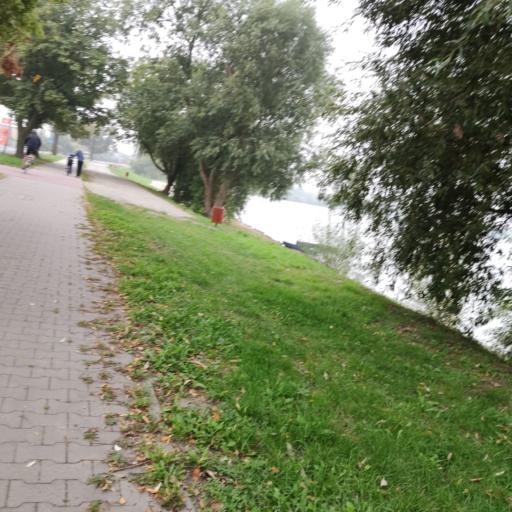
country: PL
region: Kujawsko-Pomorskie
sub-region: Powiat zninski
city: Znin
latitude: 52.8558
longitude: 17.7521
